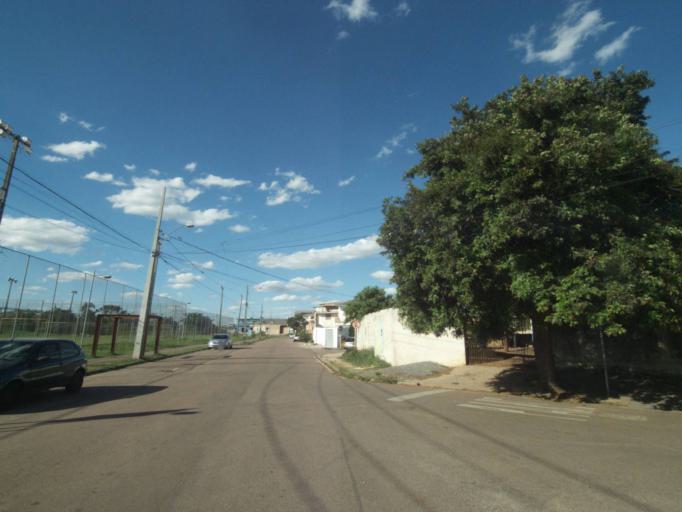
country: BR
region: Parana
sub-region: Curitiba
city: Curitiba
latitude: -25.5103
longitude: -49.3372
